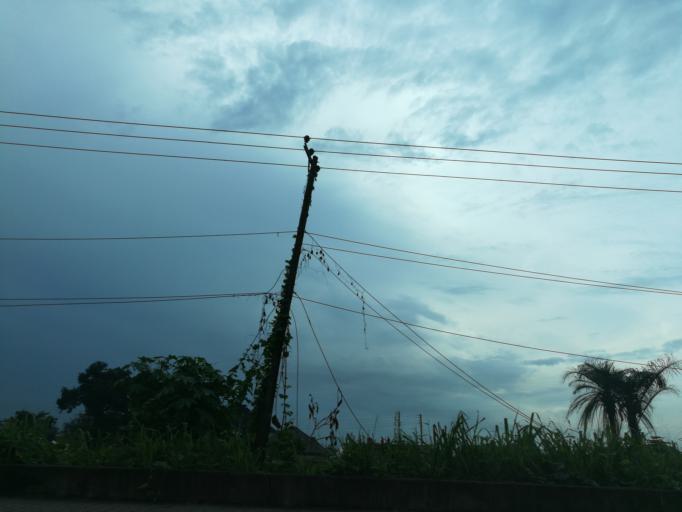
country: NG
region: Rivers
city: Port Harcourt
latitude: 4.8067
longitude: 7.0118
